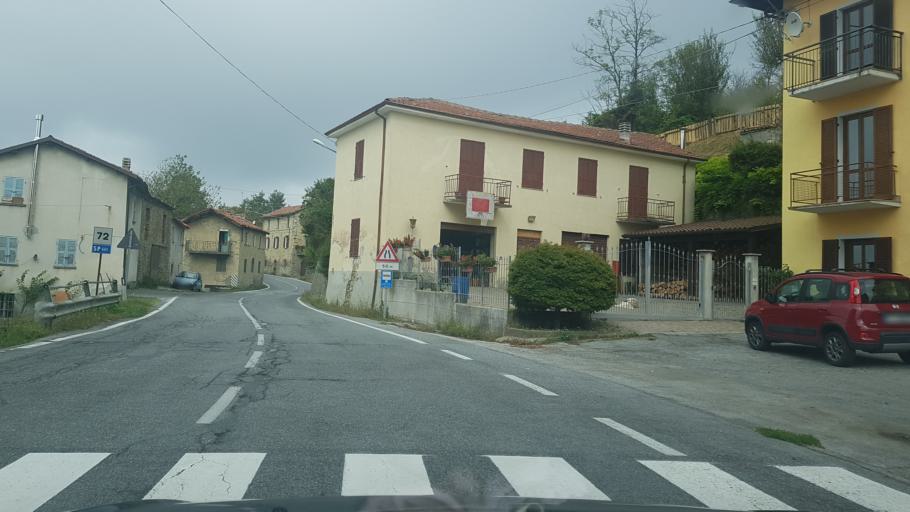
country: IT
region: Piedmont
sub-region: Provincia di Cuneo
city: Sale delle Langhe
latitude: 44.4088
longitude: 8.1059
